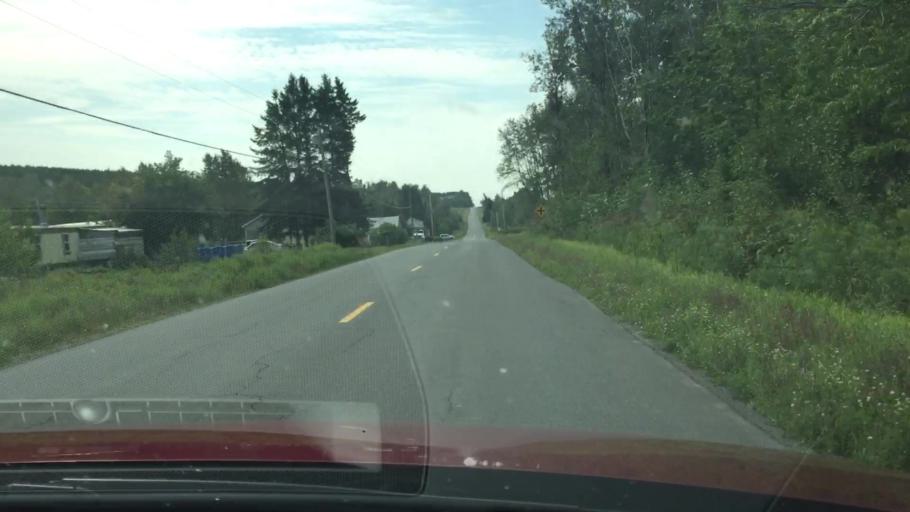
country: US
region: Maine
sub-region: Aroostook County
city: Caribou
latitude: 46.8126
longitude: -68.0244
